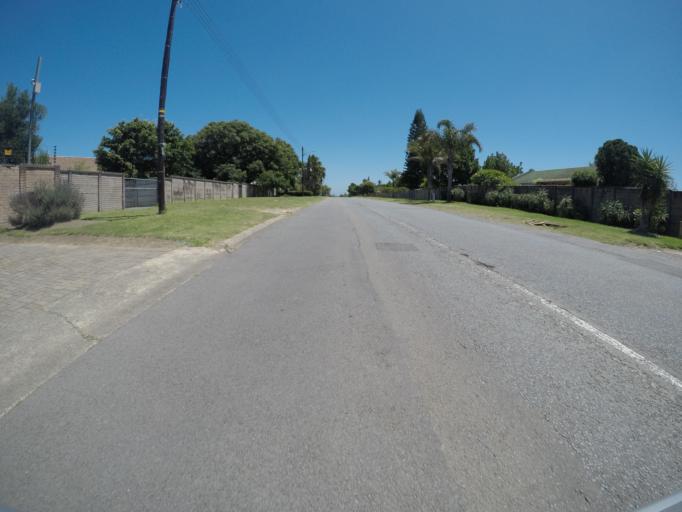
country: ZA
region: Eastern Cape
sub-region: Buffalo City Metropolitan Municipality
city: East London
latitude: -32.9566
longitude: 27.9409
